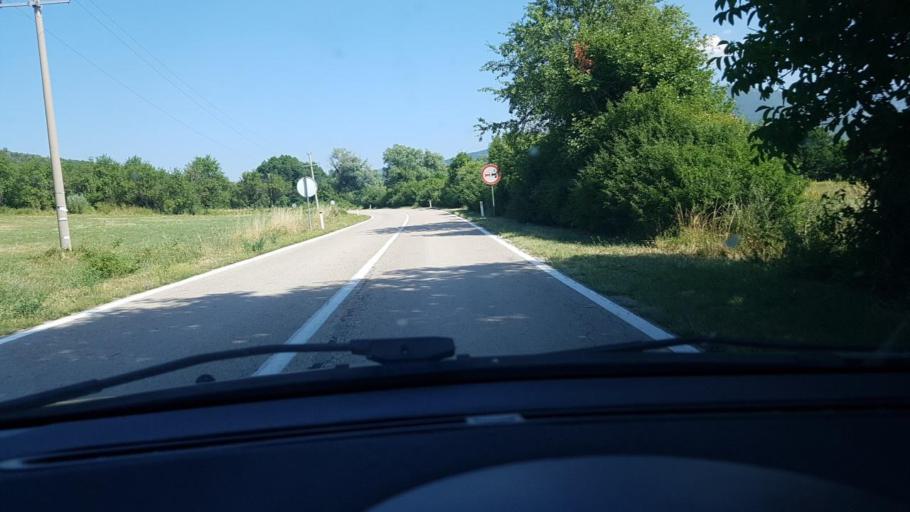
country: BA
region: Federation of Bosnia and Herzegovina
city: Bosansko Grahovo
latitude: 44.0706
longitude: 16.5762
